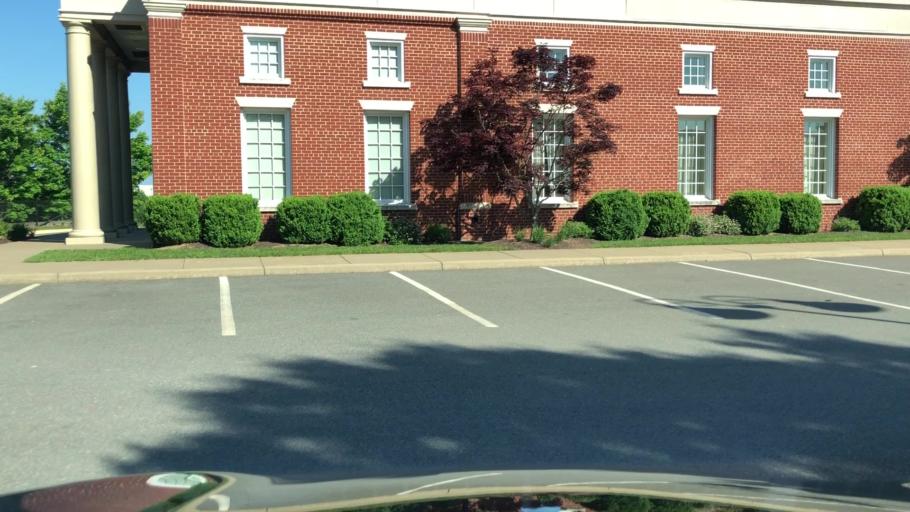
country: US
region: Virginia
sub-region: Stafford County
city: Falmouth
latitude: 38.3582
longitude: -77.5223
